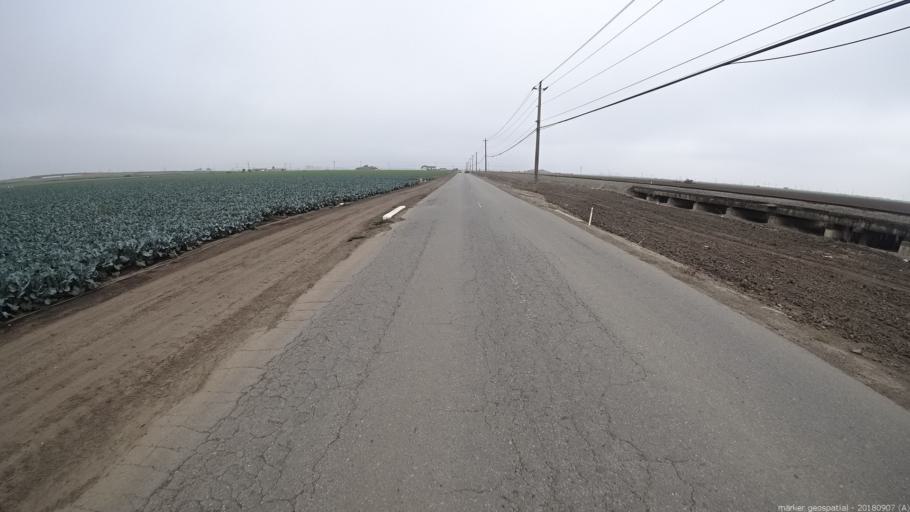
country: US
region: California
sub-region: Monterey County
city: Castroville
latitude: 36.7383
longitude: -121.7715
